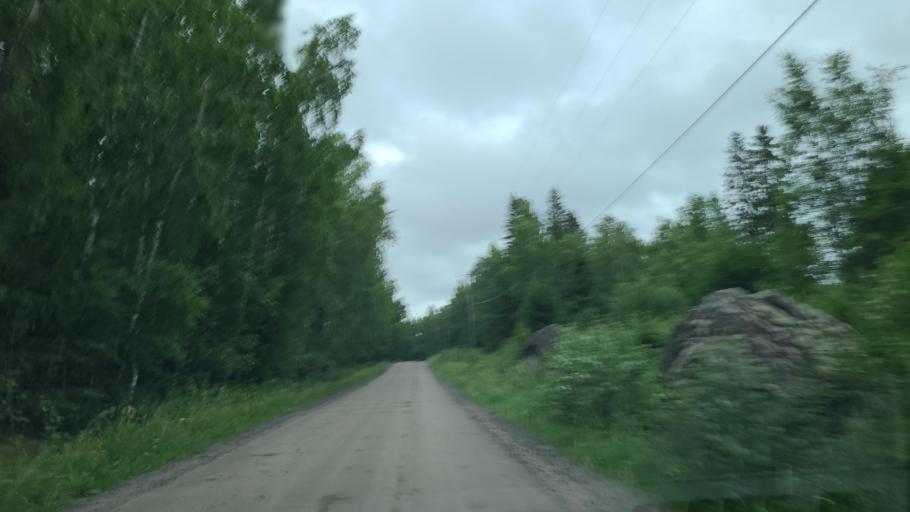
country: FI
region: Ostrobothnia
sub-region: Vaasa
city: Replot
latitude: 63.3071
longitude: 21.1553
